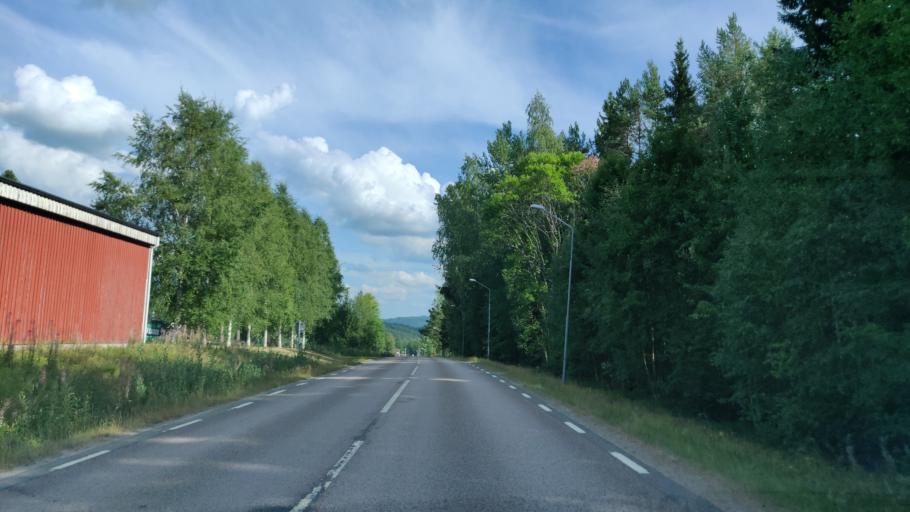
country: SE
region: Vaermland
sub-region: Hagfors Kommun
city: Hagfors
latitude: 60.0684
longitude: 13.6354
